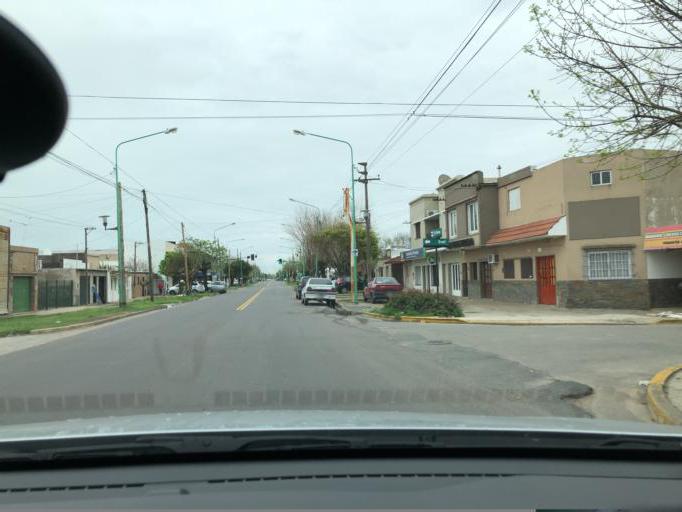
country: AR
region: Buenos Aires
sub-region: Partido de Ensenada
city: Ensenada
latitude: -34.8590
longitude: -57.9145
